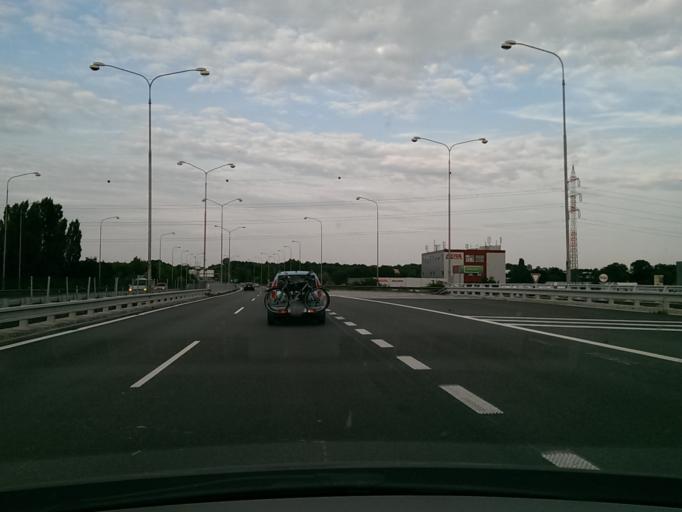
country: CZ
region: South Moravian
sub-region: Mesto Brno
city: Brno
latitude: 49.1595
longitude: 16.6336
